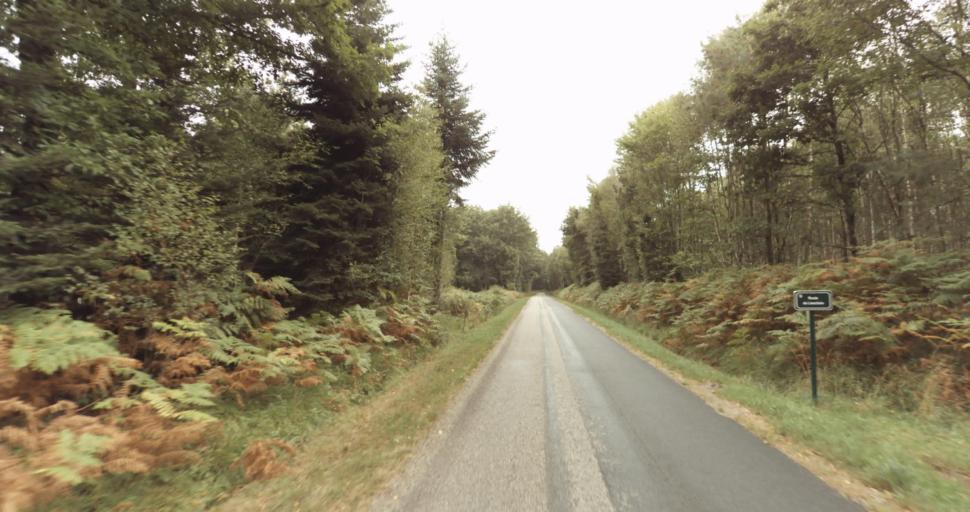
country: FR
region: Lower Normandy
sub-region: Departement de l'Orne
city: Gace
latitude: 48.8271
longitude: 0.3375
